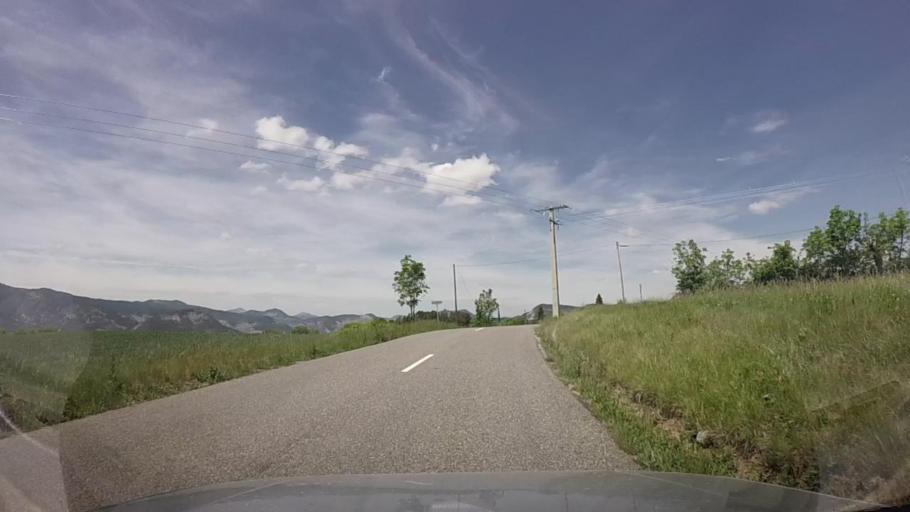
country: FR
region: Provence-Alpes-Cote d'Azur
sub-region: Departement des Alpes-de-Haute-Provence
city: Seyne-les-Alpes
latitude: 44.3812
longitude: 6.3484
